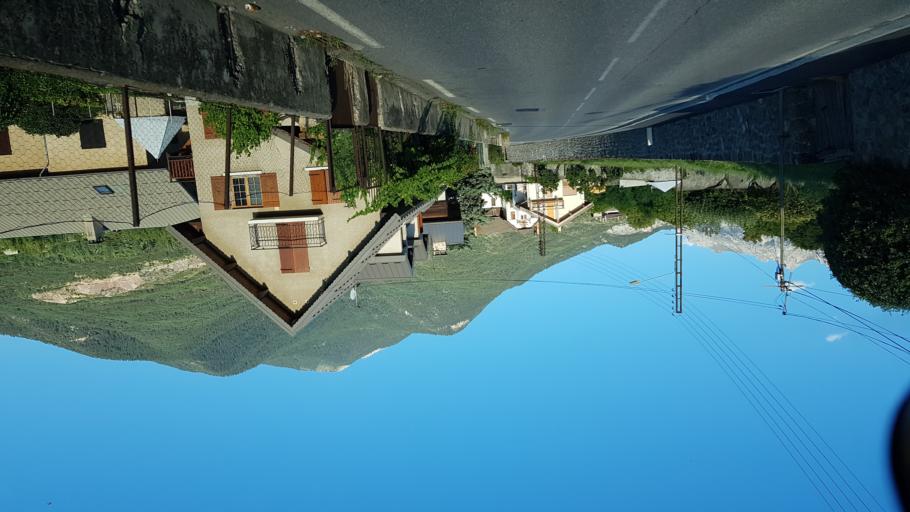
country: FR
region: Provence-Alpes-Cote d'Azur
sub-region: Departement des Hautes-Alpes
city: Guillestre
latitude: 44.6601
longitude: 6.6461
